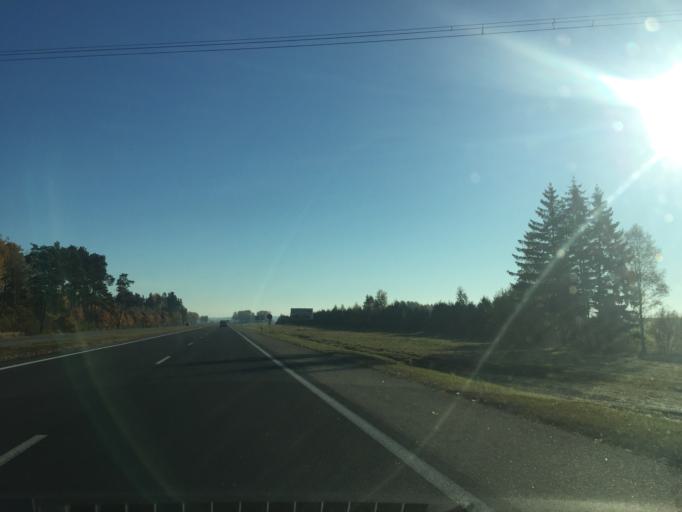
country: BY
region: Minsk
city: Smilavichy
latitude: 53.7639
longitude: 28.1130
